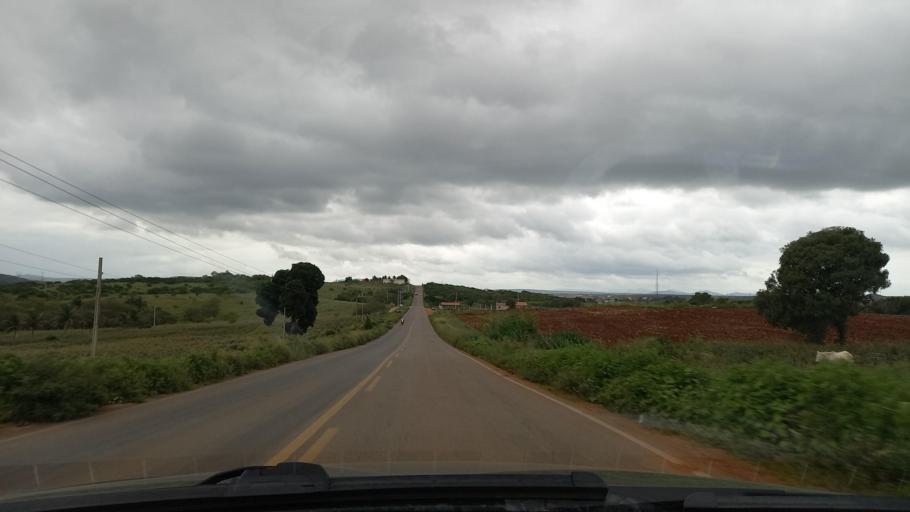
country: BR
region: Sergipe
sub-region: Caninde De Sao Francisco
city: Caninde de Sao Francisco
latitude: -9.6764
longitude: -37.8026
